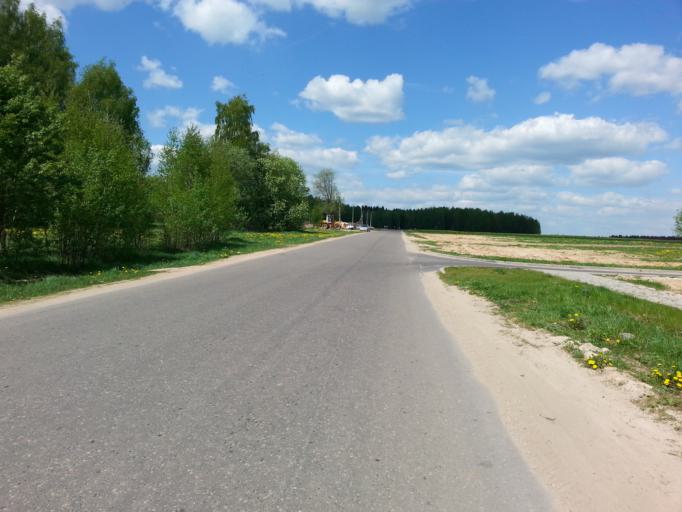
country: BY
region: Minsk
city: Narach
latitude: 54.9156
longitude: 26.6956
